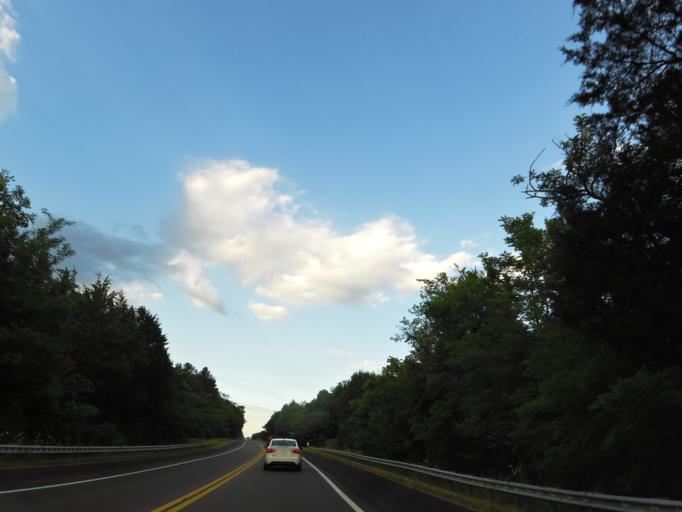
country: US
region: Tennessee
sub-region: Maury County
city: Spring Hill
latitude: 35.6381
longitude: -86.9146
